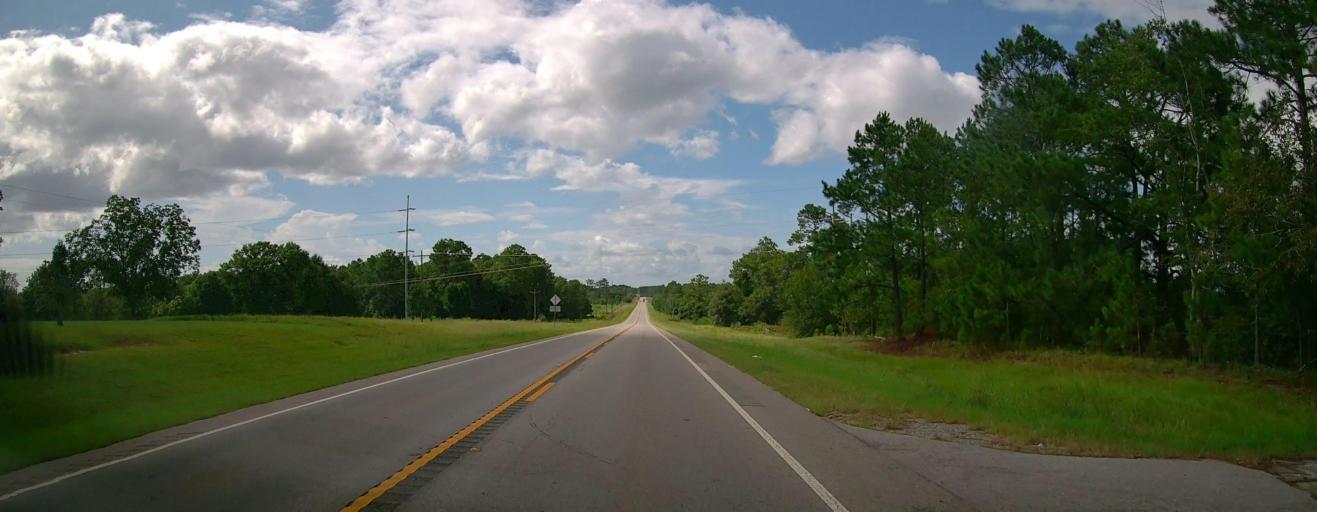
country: US
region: Georgia
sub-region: Coffee County
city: Douglas
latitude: 31.5303
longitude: -82.8792
